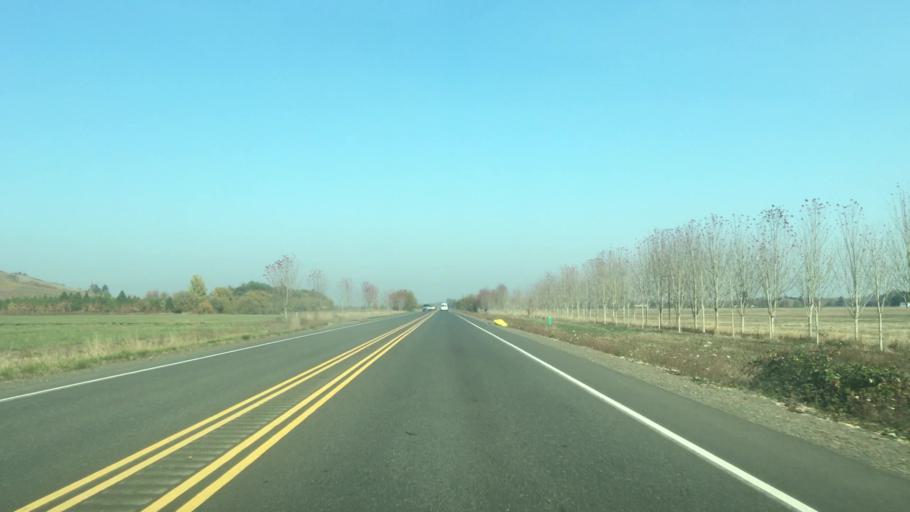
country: US
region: Oregon
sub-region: Yamhill County
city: Amity
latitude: 45.1376
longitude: -123.2893
